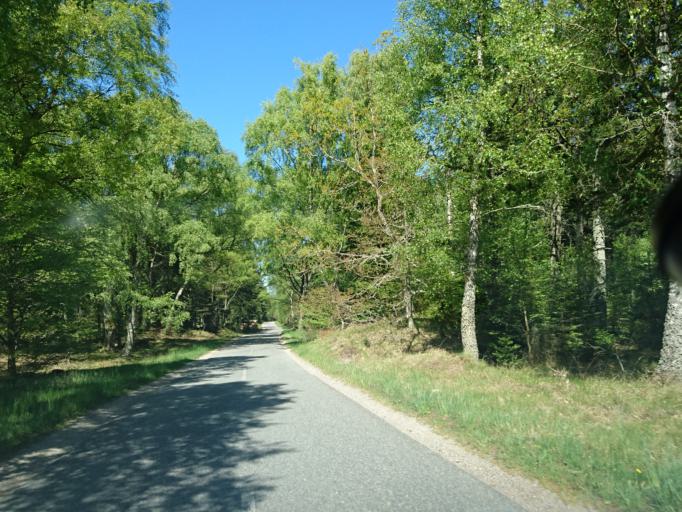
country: DK
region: North Denmark
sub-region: Hjorring Kommune
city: Sindal
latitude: 57.5925
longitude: 10.2300
